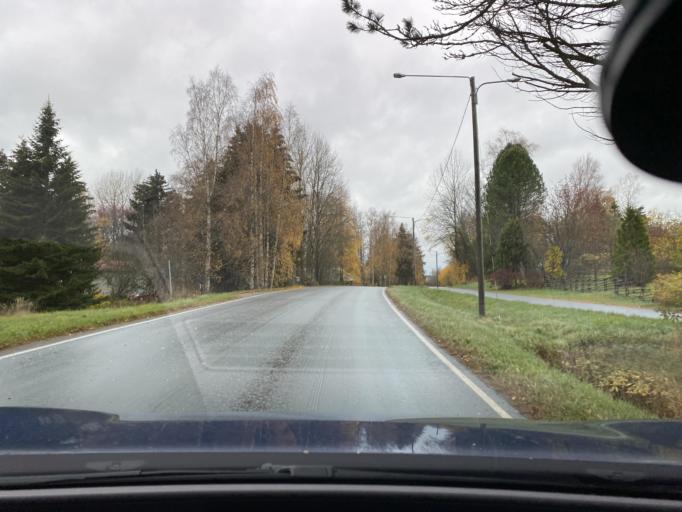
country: FI
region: Satakunta
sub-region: Pori
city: Kokemaeki
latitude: 61.2578
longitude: 22.3891
